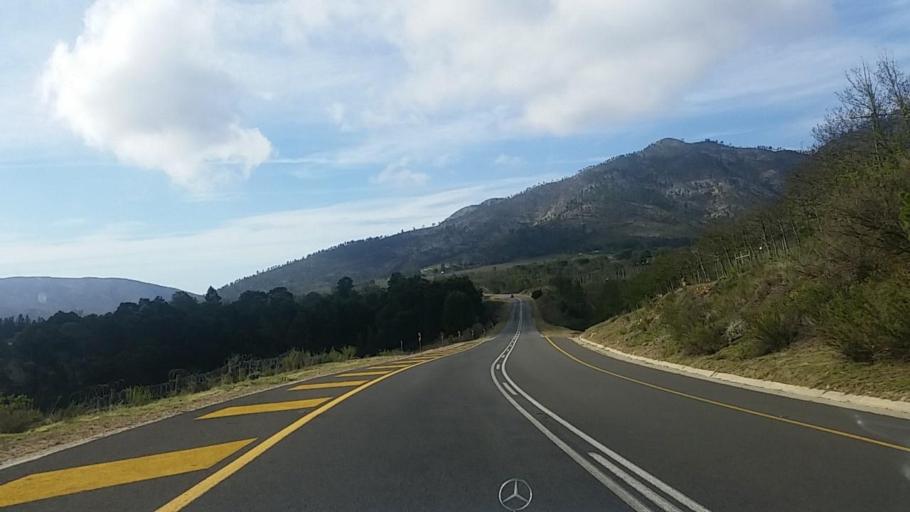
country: ZA
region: Western Cape
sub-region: Eden District Municipality
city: George
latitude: -33.8620
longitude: 22.3599
